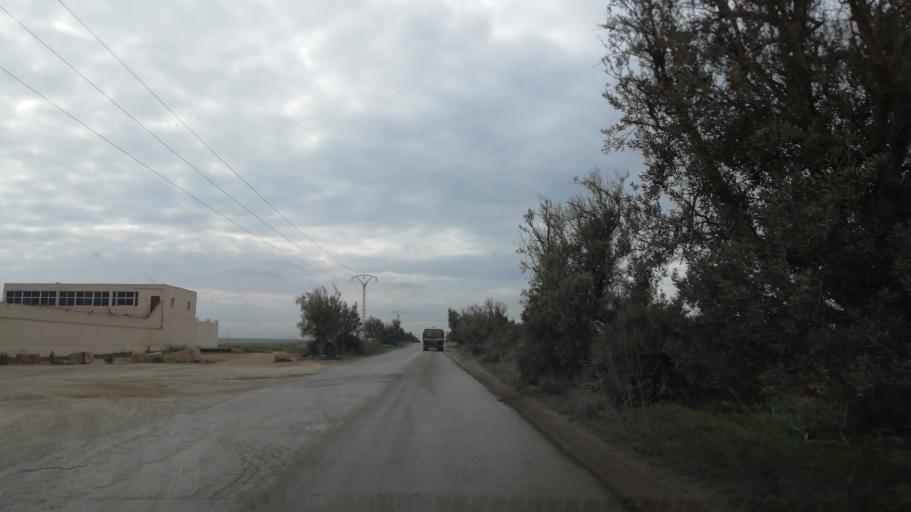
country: DZ
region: Oran
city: Ain el Bya
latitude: 35.7807
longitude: -0.3447
